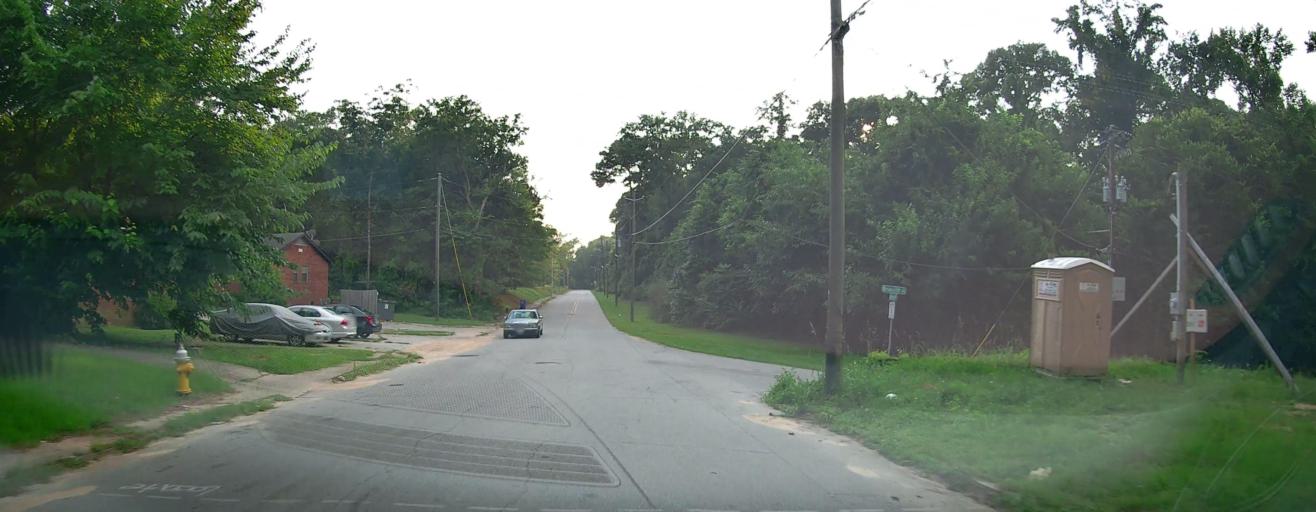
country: US
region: Georgia
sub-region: Bibb County
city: Macon
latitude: 32.8580
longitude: -83.6213
